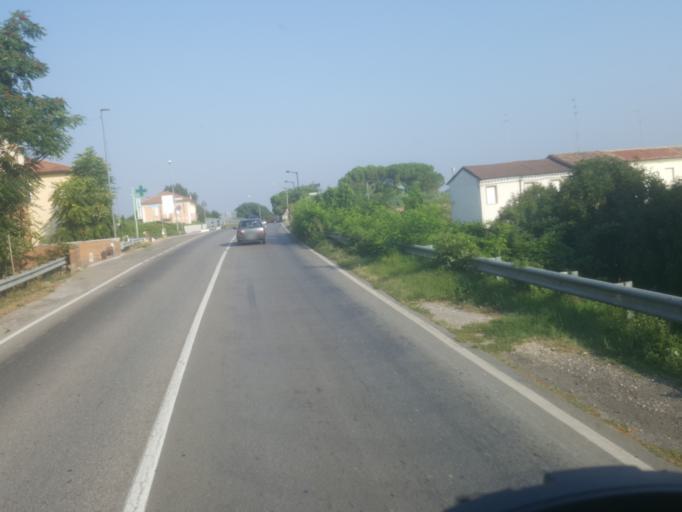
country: IT
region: Emilia-Romagna
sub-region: Provincia di Ravenna
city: Mezzano
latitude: 44.4689
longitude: 12.0838
